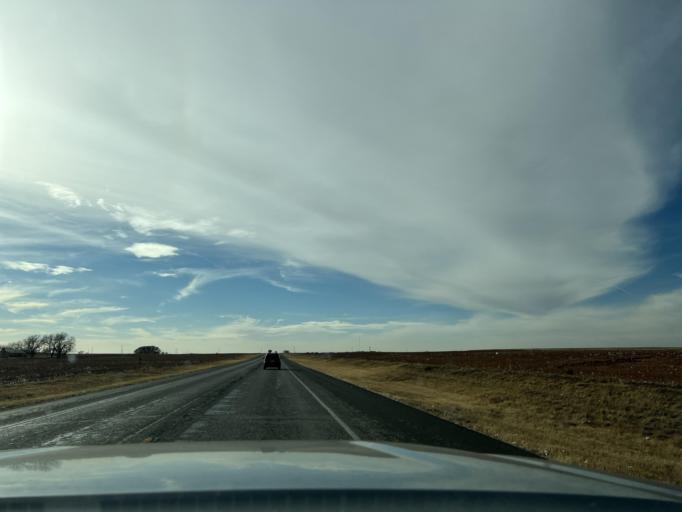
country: US
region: Texas
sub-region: Fisher County
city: Roby
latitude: 32.7532
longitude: -100.3398
